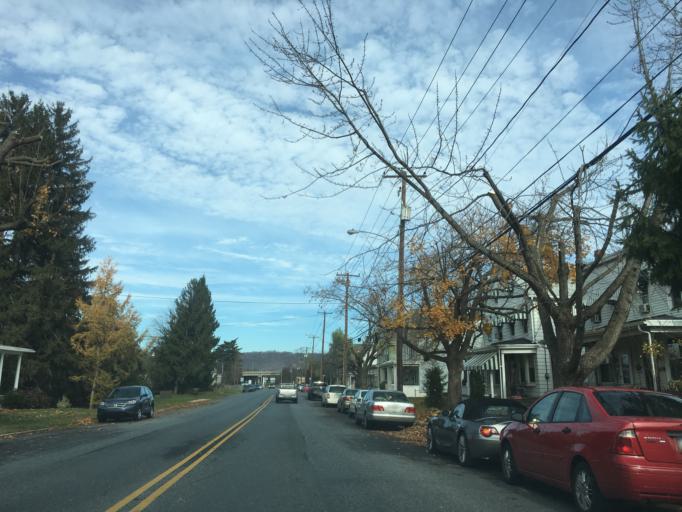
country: US
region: Pennsylvania
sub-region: Dauphin County
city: Harrisburg
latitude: 40.3060
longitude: -76.8950
